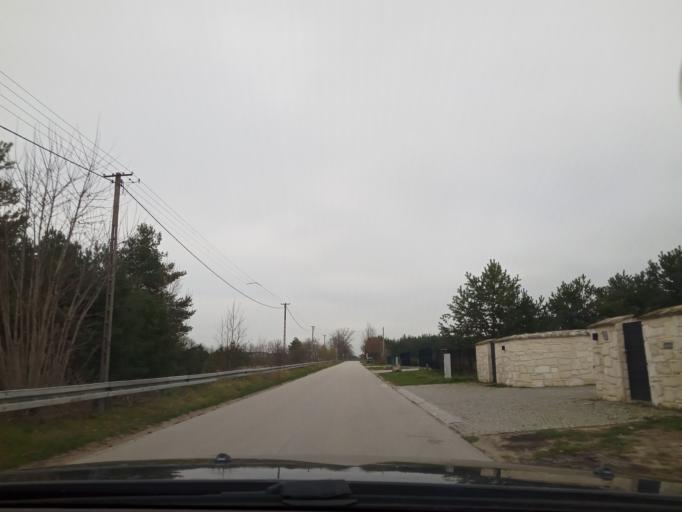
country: PL
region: Swietokrzyskie
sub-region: Powiat jedrzejowski
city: Imielno
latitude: 50.5911
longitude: 20.4780
